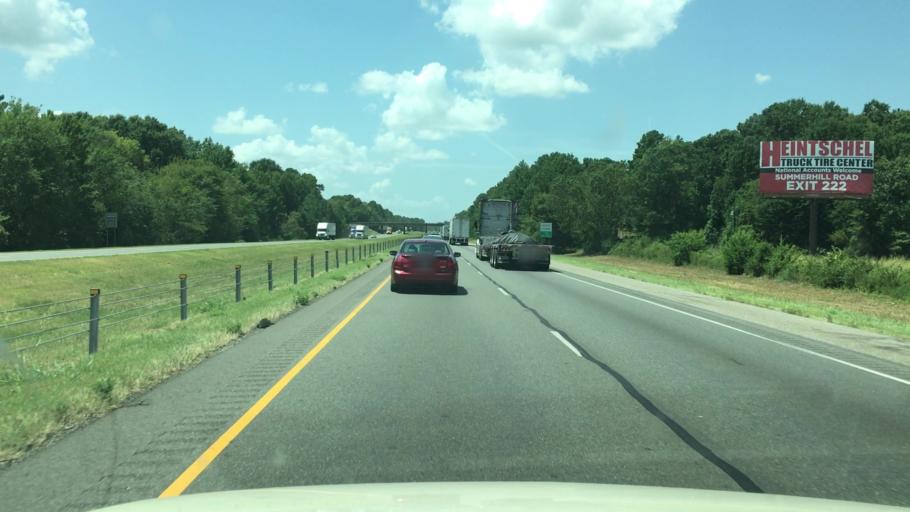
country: US
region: Arkansas
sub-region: Miller County
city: Texarkana
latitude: 33.4918
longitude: -93.9686
